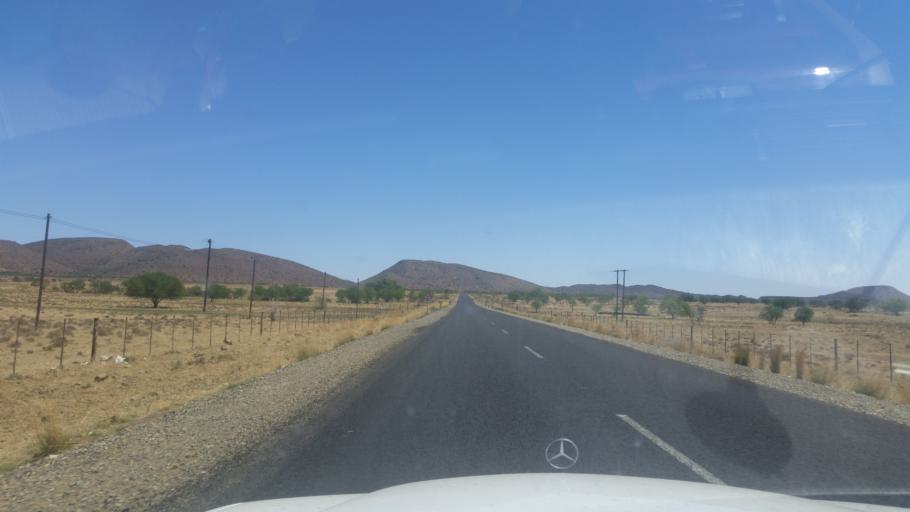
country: ZA
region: Northern Cape
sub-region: Pixley ka Seme District Municipality
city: Colesberg
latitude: -30.6321
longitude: 25.4474
